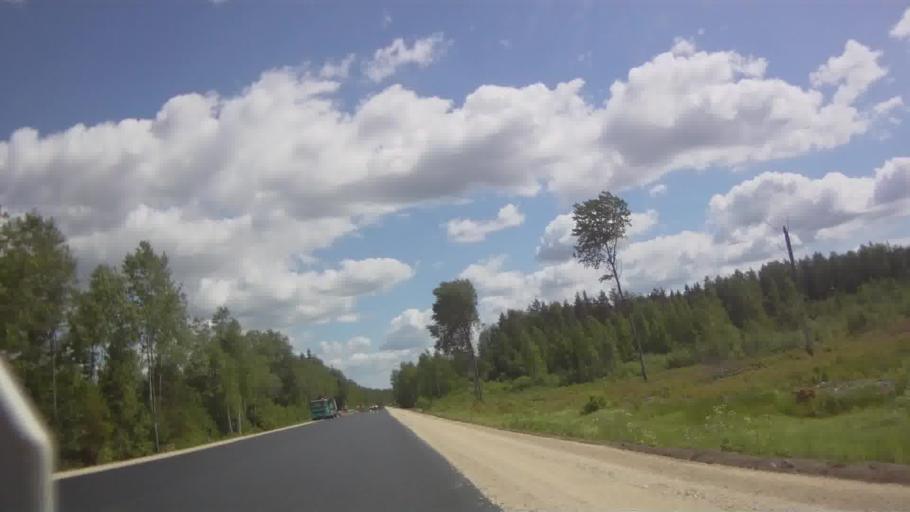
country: LV
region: Vilanu
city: Vilani
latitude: 56.5630
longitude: 27.0096
